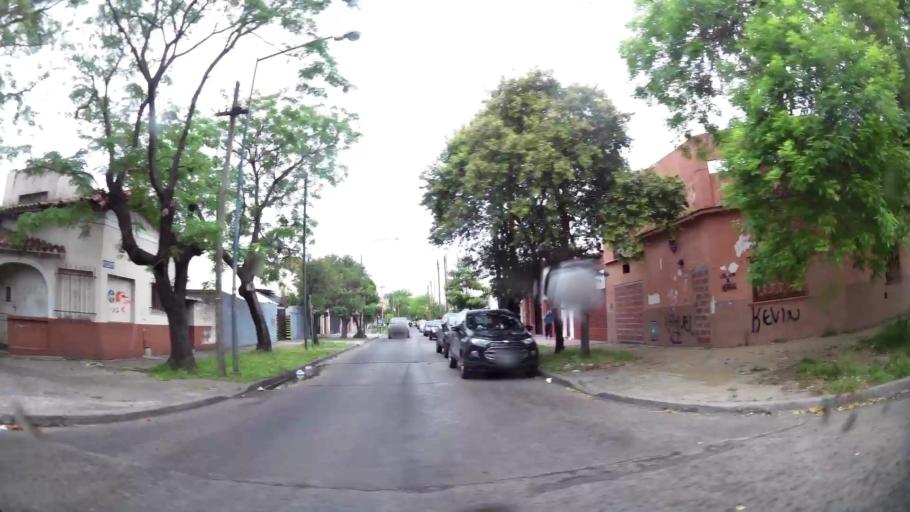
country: AR
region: Buenos Aires
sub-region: Partido de Lanus
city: Lanus
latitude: -34.6946
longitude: -58.4004
